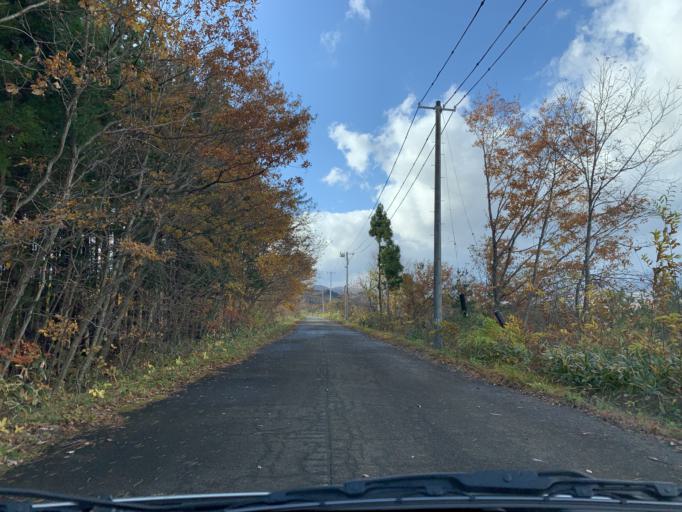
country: JP
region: Iwate
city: Mizusawa
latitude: 39.1041
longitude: 140.9742
